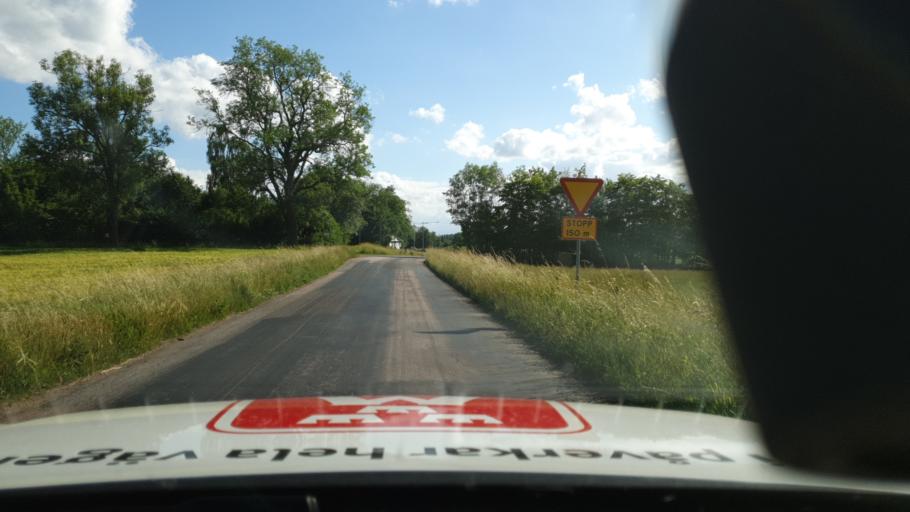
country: SE
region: Vaestra Goetaland
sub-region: Skara Kommun
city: Axvall
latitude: 58.3912
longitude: 13.6523
